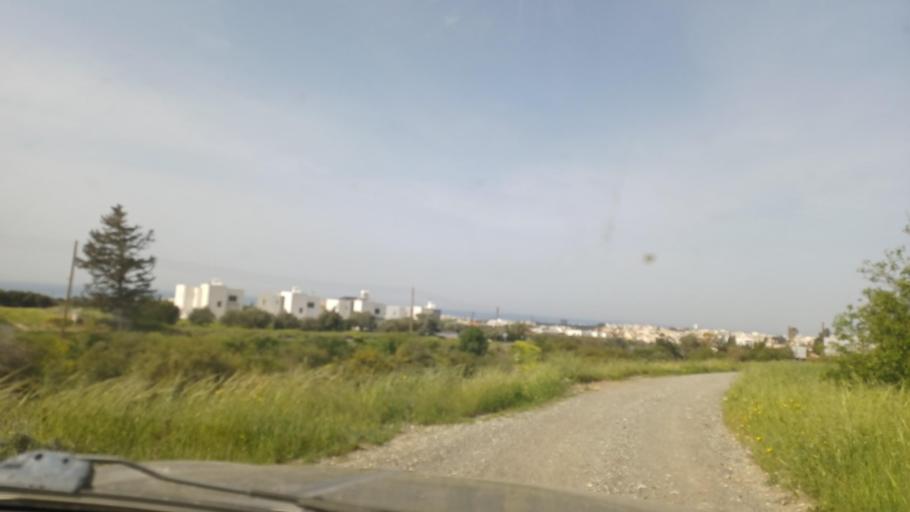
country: CY
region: Pafos
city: Paphos
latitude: 34.7587
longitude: 32.4707
